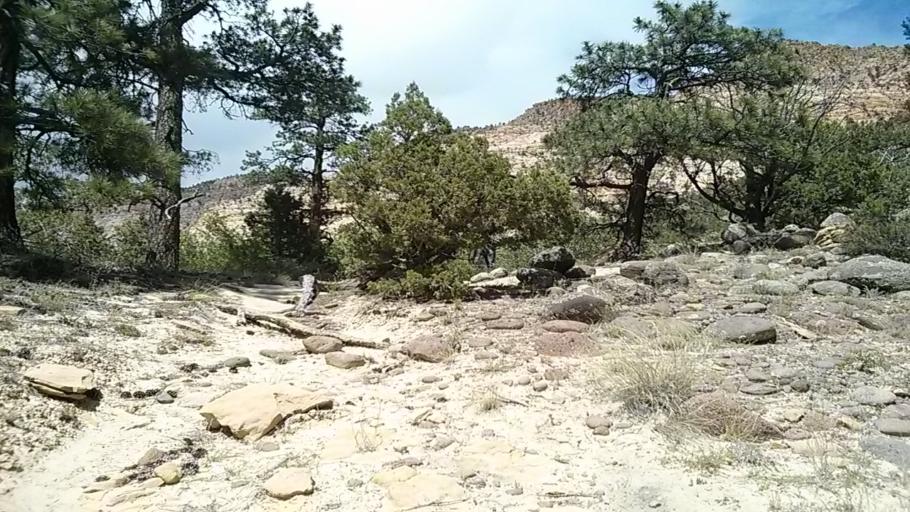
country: US
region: Utah
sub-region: Wayne County
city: Loa
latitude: 37.8648
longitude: -111.6341
